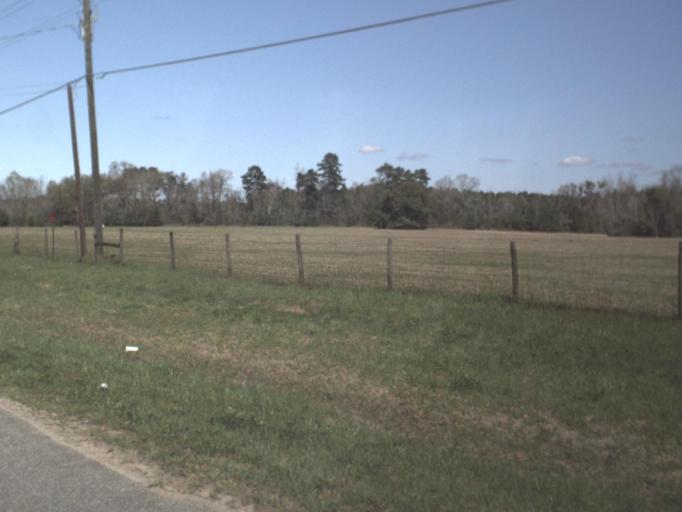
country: US
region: Florida
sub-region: Gadsden County
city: Gretna
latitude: 30.6692
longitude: -84.6130
